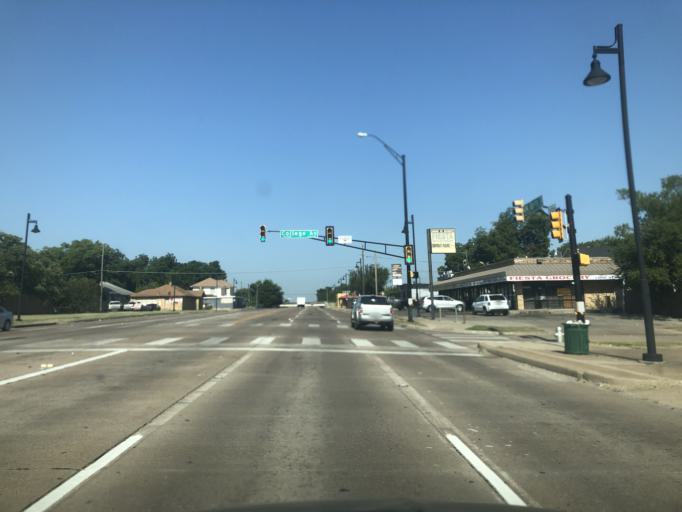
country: US
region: Texas
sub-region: Tarrant County
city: Fort Worth
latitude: 32.7061
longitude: -97.3352
